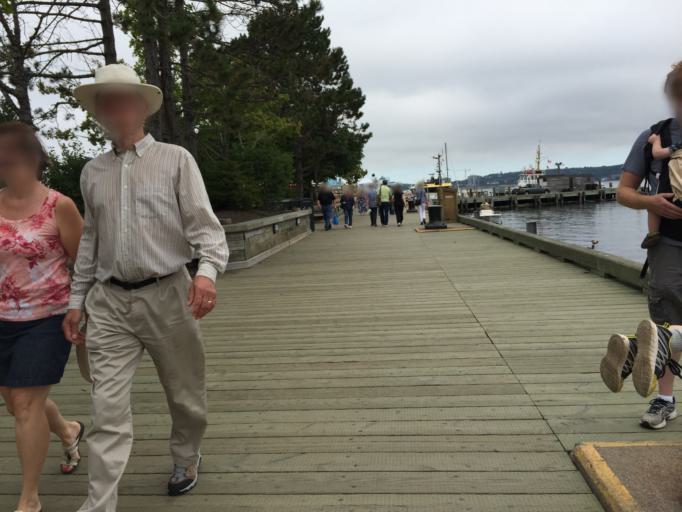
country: CA
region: Nova Scotia
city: Halifax
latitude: 44.6461
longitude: -63.5694
